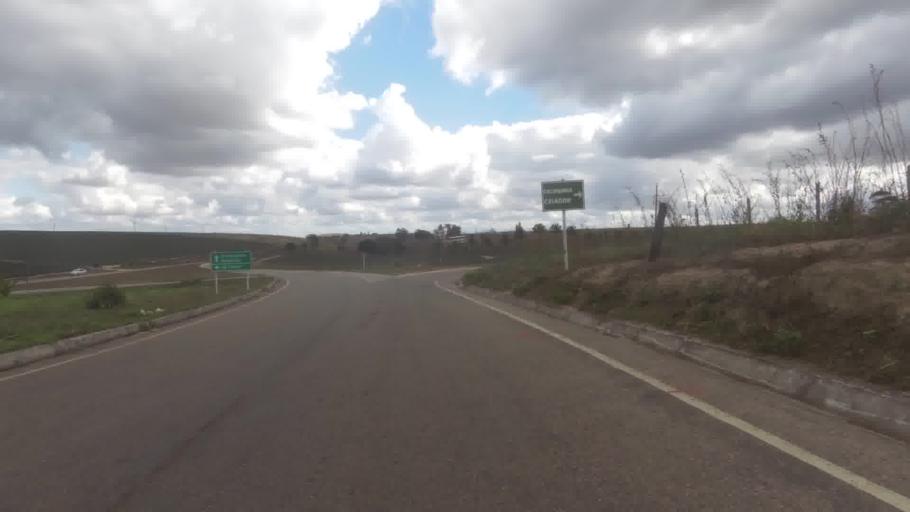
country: BR
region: Espirito Santo
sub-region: Marataizes
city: Marataizes
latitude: -21.1723
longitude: -40.9877
